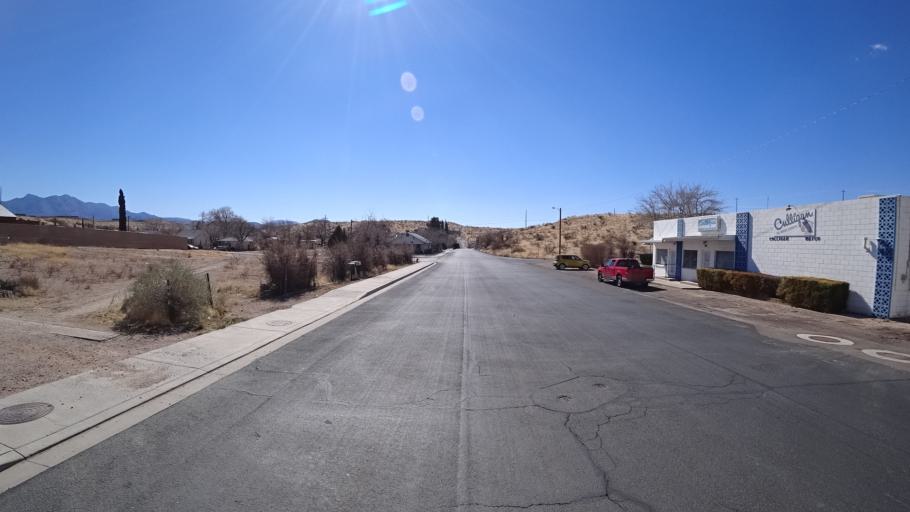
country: US
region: Arizona
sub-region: Mohave County
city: Kingman
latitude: 35.1873
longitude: -114.0532
